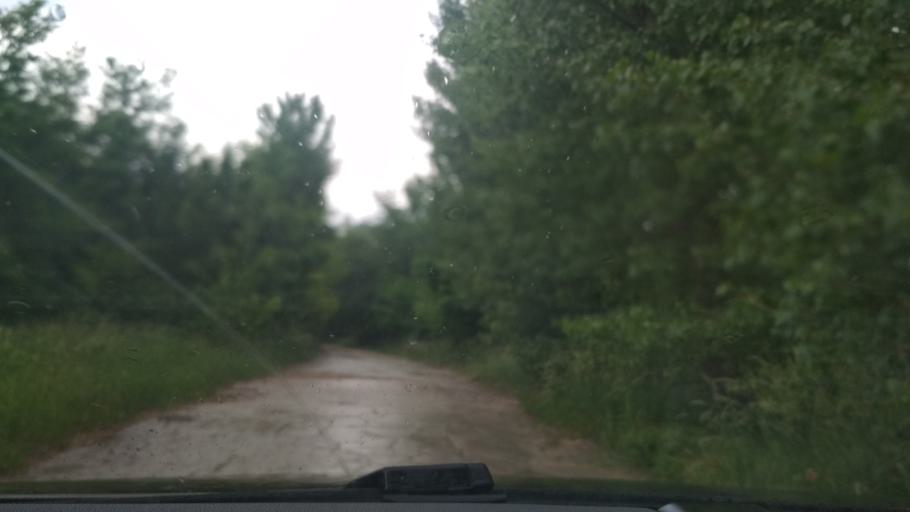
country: MD
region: Singerei
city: Biruinta
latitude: 47.7474
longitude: 28.1395
